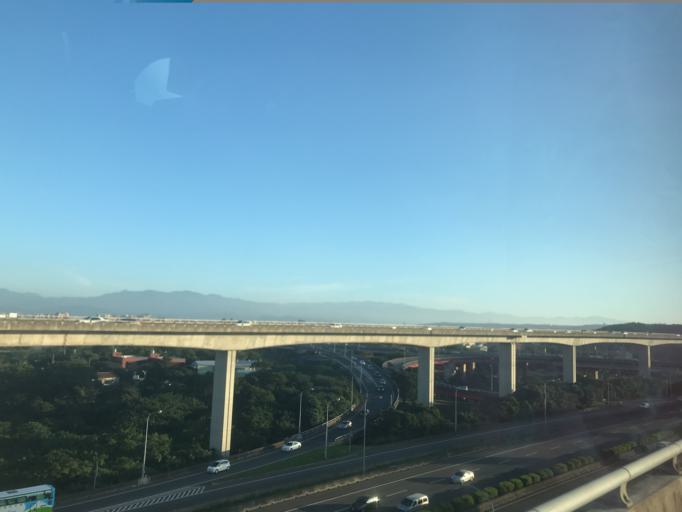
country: TW
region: Taiwan
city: Daxi
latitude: 24.9387
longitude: 121.1915
